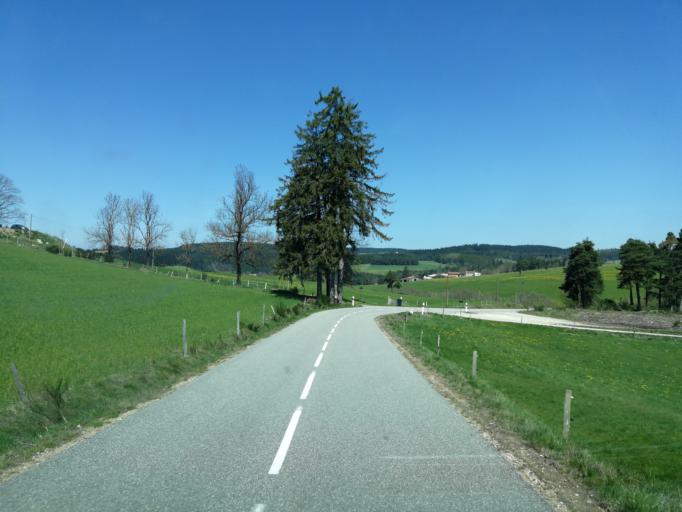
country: FR
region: Rhone-Alpes
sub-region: Departement de la Loire
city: Marlhes
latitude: 45.2917
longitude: 4.3873
